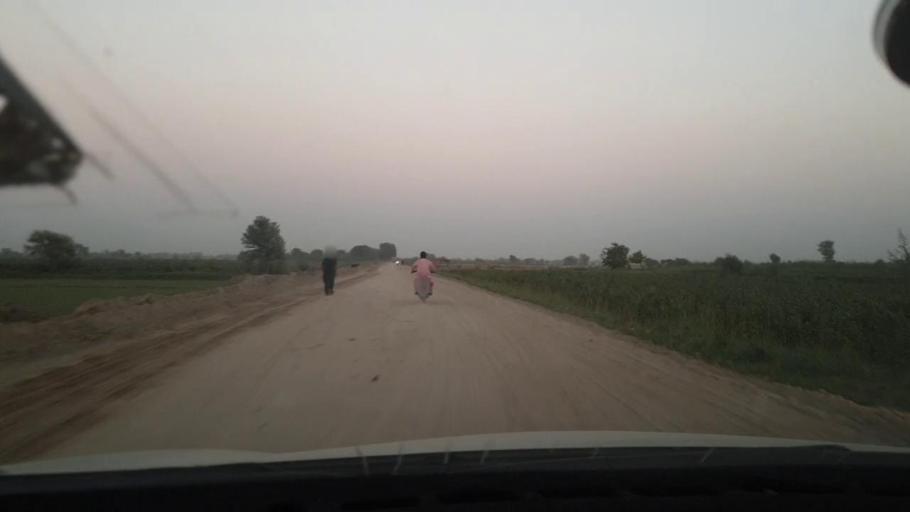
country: PK
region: Sindh
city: Tando Adam
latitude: 25.7533
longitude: 68.6009
